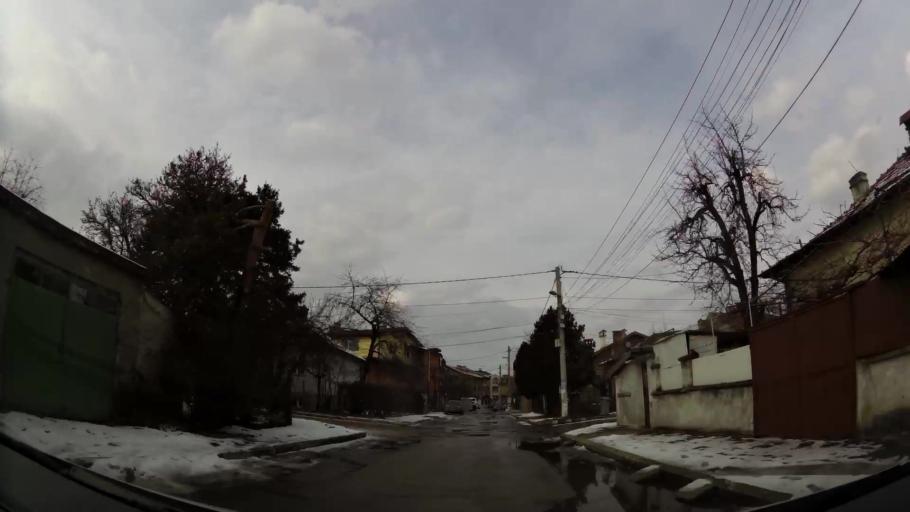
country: BG
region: Sofia-Capital
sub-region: Stolichna Obshtina
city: Sofia
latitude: 42.7037
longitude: 23.3836
